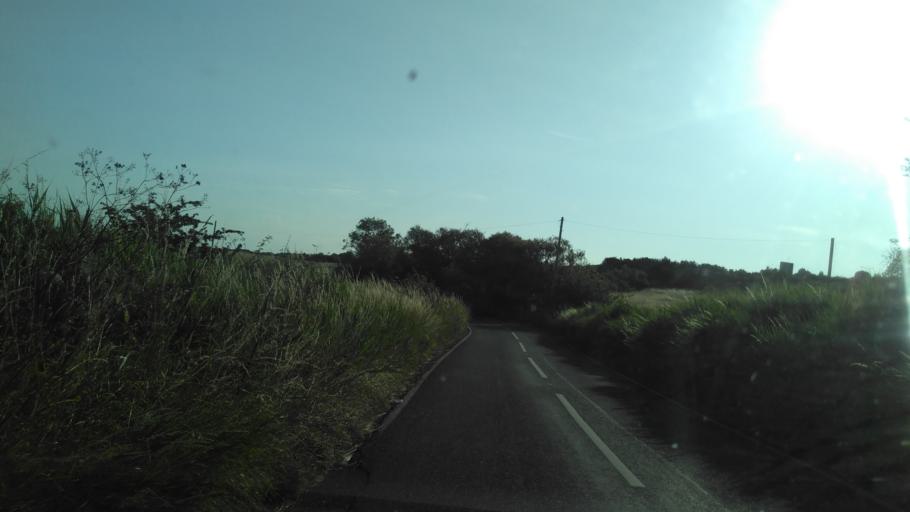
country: GB
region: England
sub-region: Kent
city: Whitstable
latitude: 51.3350
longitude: 0.9991
